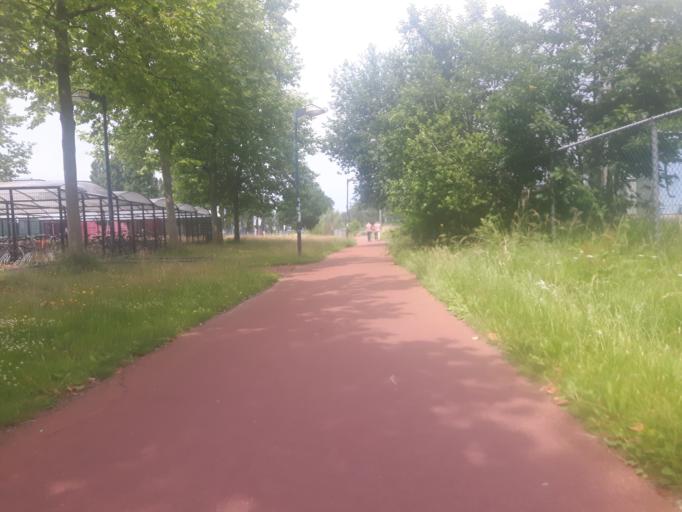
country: NL
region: Overijssel
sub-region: Gemeente Hengelo
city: Hengelo
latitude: 52.2379
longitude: 6.8377
